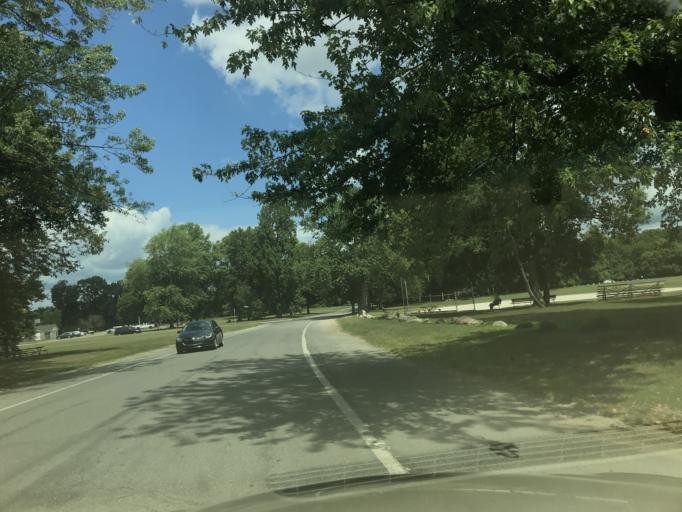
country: US
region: Michigan
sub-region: Jackson County
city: Jackson
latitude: 42.2159
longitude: -84.4158
